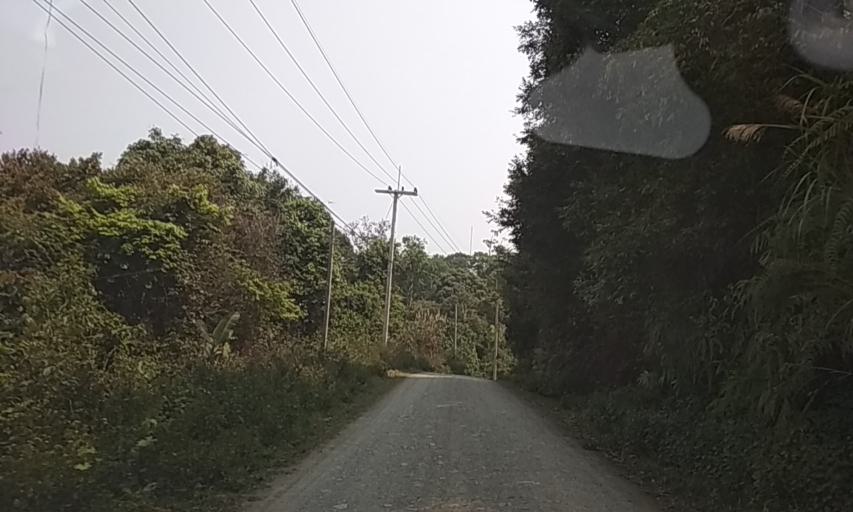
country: TH
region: Nan
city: Chaloem Phra Kiat
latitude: 20.0345
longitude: 101.0932
